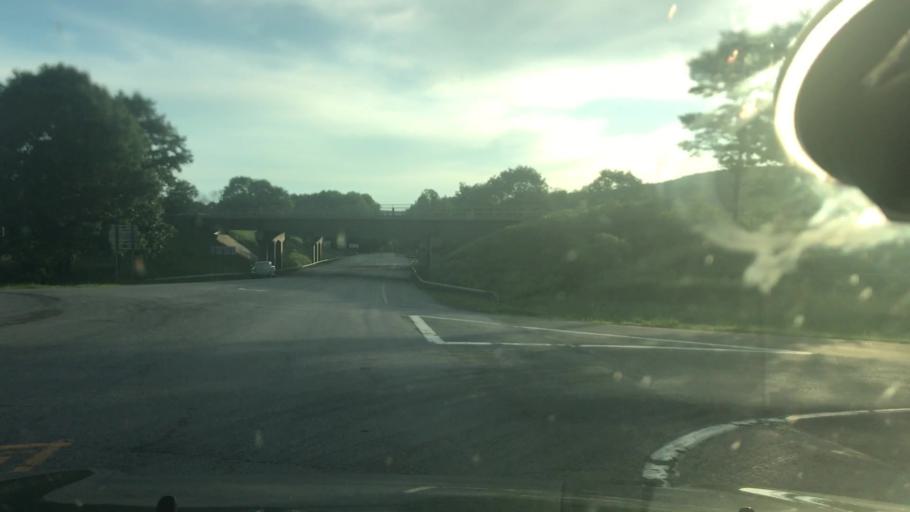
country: US
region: New York
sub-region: Otsego County
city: Unadilla
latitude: 42.3331
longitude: -75.2777
